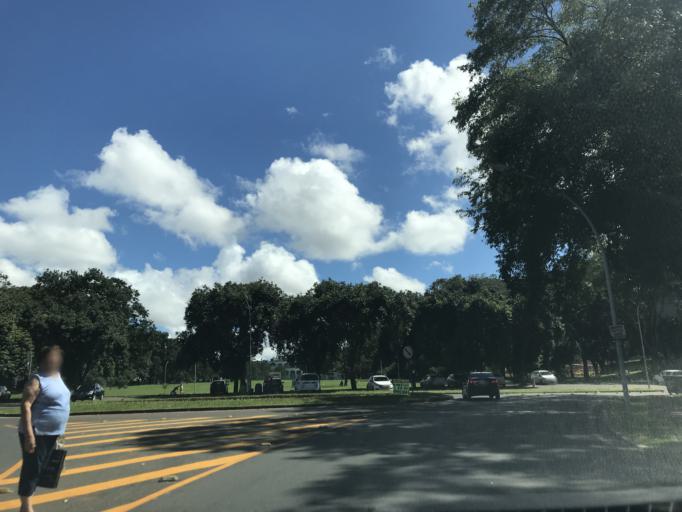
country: BR
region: Federal District
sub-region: Brasilia
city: Brasilia
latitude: -15.8222
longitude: -47.9016
